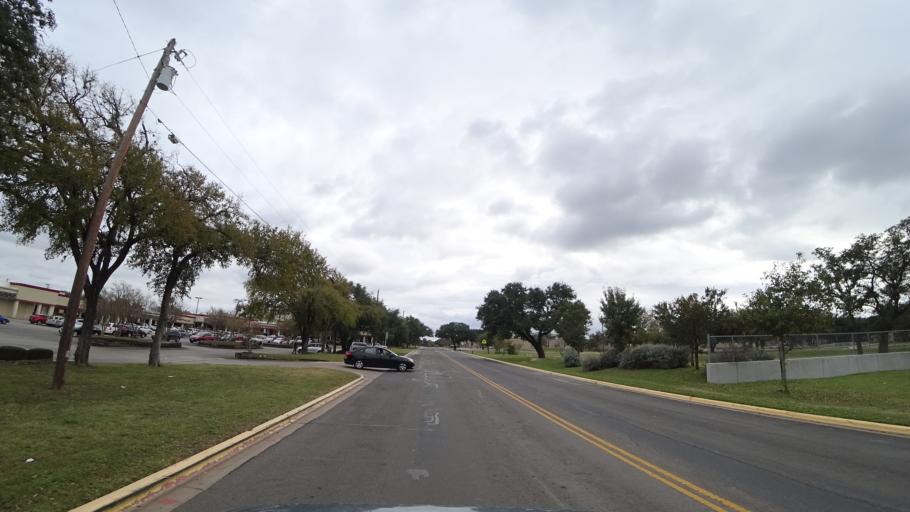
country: US
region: Texas
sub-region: Williamson County
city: Round Rock
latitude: 30.5113
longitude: -97.6952
